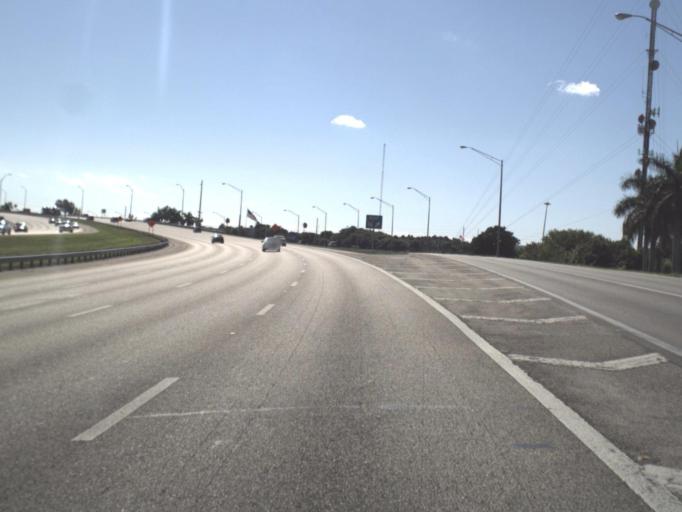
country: US
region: Florida
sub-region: Miami-Dade County
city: Three Lakes
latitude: 25.6339
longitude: -80.3853
